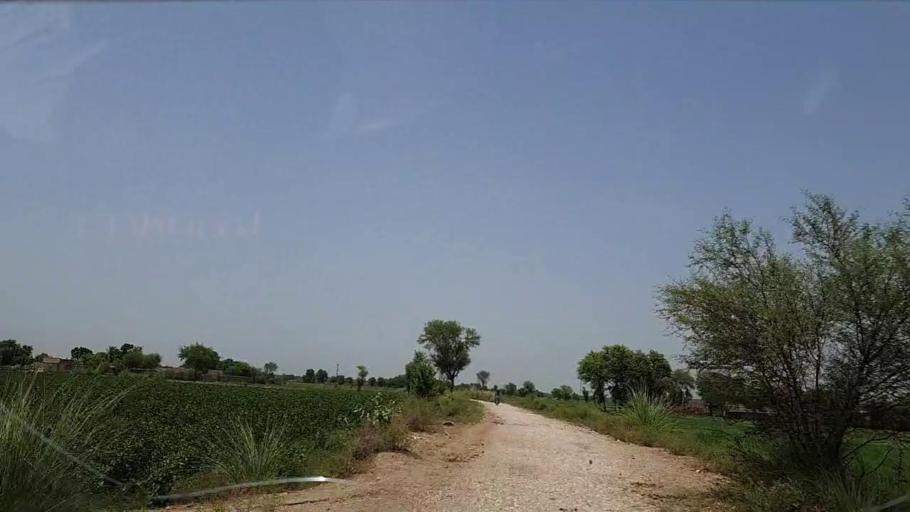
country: PK
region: Sindh
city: Tharu Shah
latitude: 26.9473
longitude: 68.0444
